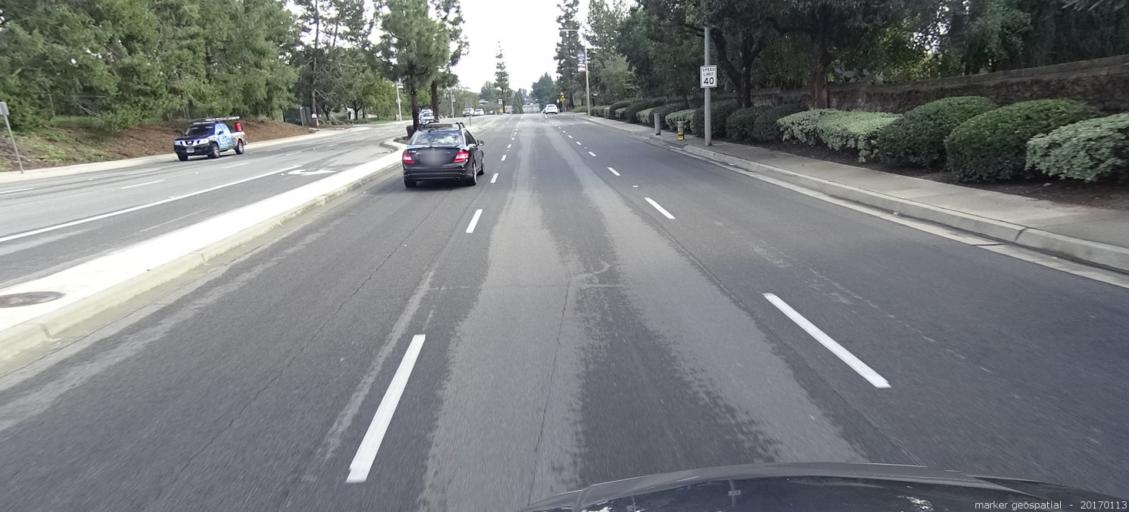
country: US
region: California
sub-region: Orange County
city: Yorba Linda
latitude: 33.8886
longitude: -117.8014
